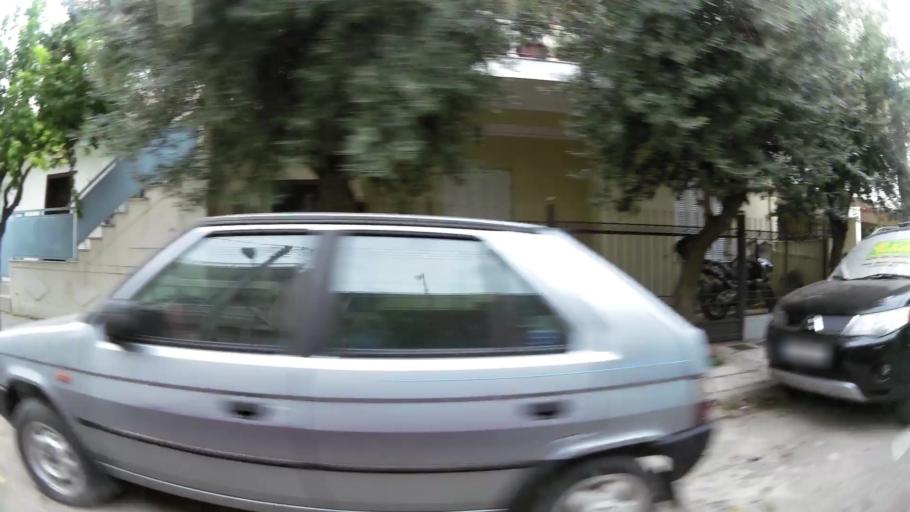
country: GR
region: Attica
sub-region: Nomarchia Athinas
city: Agioi Anargyroi
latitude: 38.0125
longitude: 23.7147
